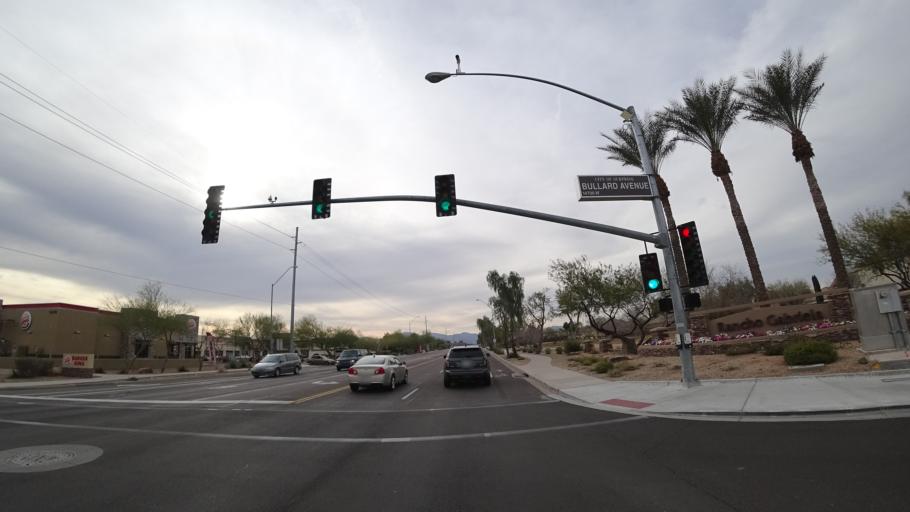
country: US
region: Arizona
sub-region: Maricopa County
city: El Mirage
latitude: 33.5949
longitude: -112.3765
